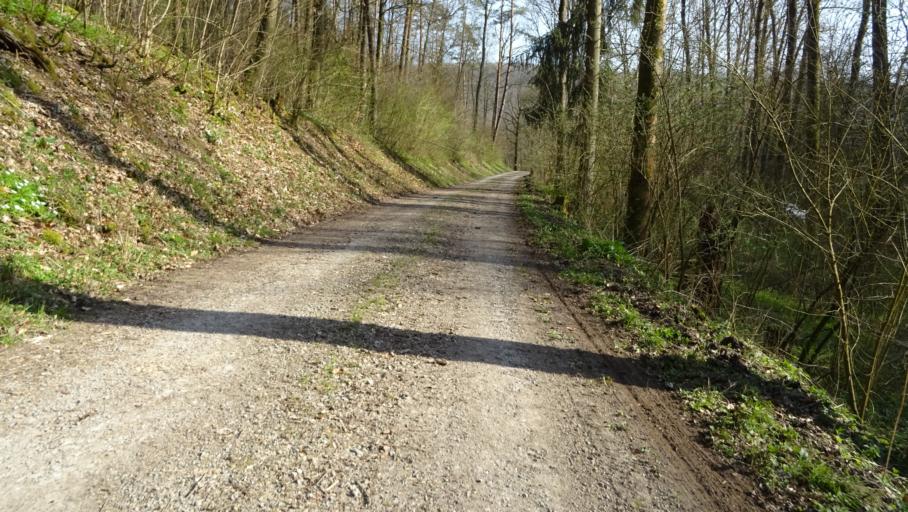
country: DE
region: Baden-Wuerttemberg
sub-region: Regierungsbezirk Stuttgart
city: Roigheim
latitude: 49.3732
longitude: 9.3589
